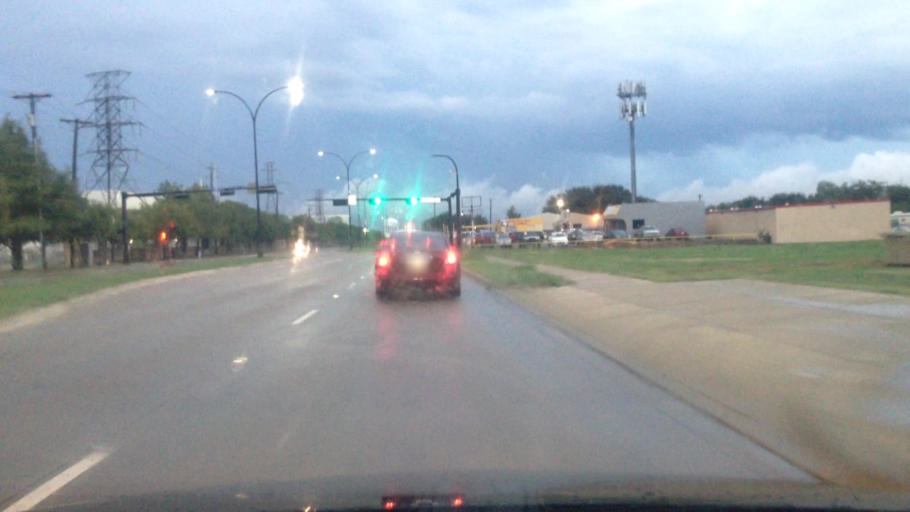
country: US
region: Texas
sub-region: Tarrant County
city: Arlington
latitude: 32.7353
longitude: -97.0764
